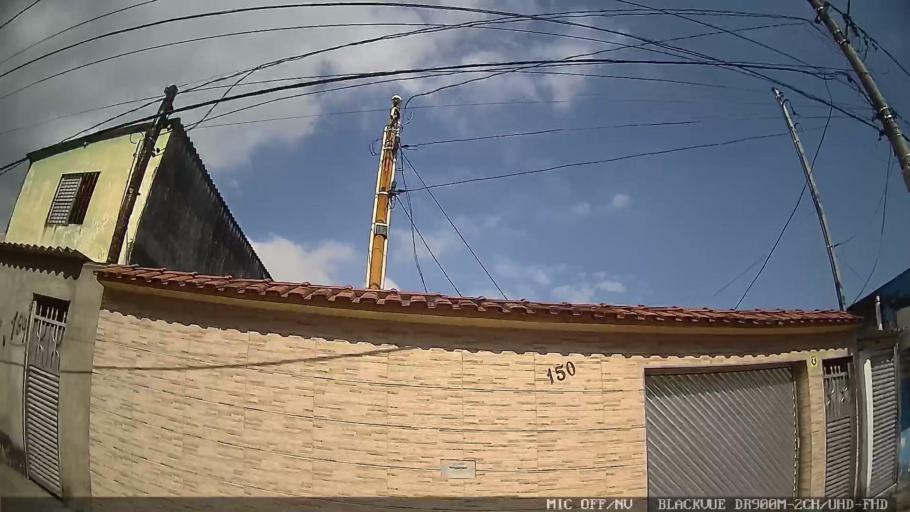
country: BR
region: Sao Paulo
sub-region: Santos
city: Santos
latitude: -23.9467
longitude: -46.2987
